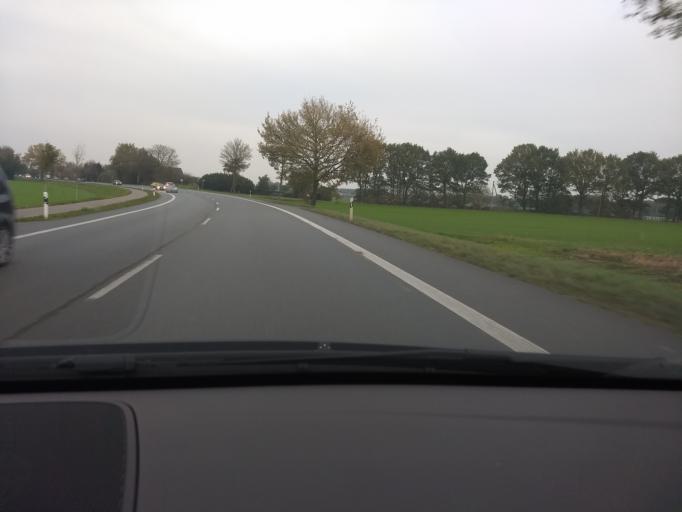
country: DE
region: North Rhine-Westphalia
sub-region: Regierungsbezirk Munster
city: Raesfeld
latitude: 51.7589
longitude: 6.8593
